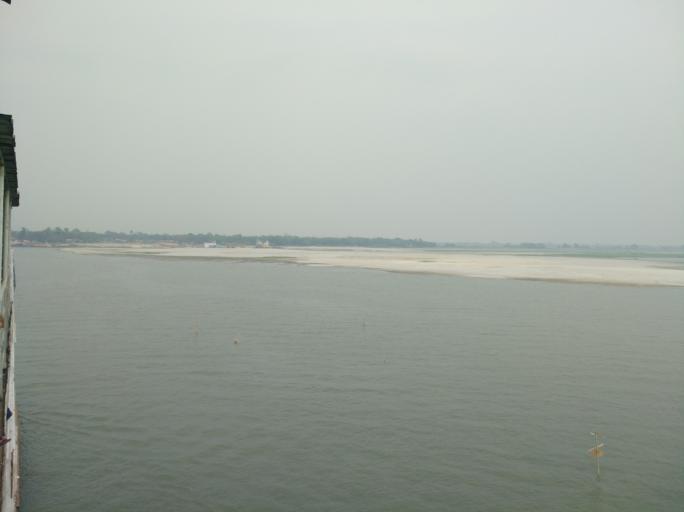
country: BD
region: Dhaka
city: Faridpur
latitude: 23.7805
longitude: 89.8072
